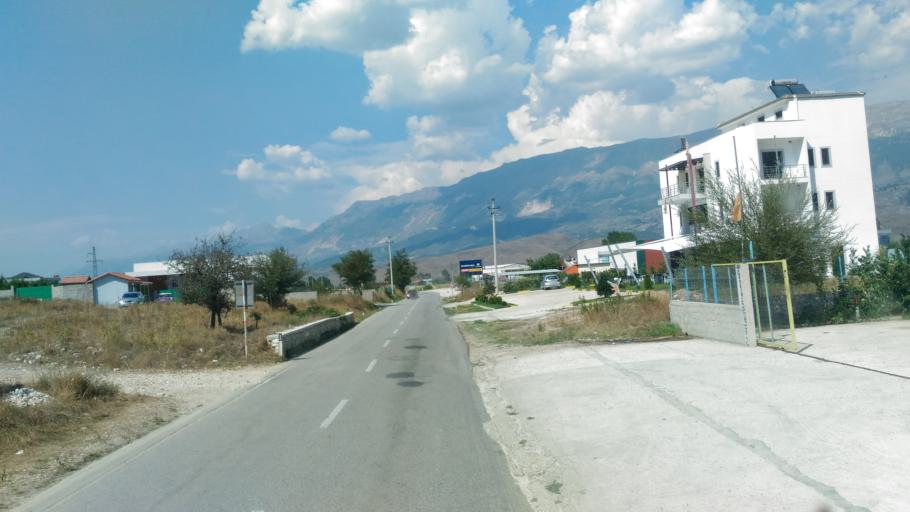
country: AL
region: Gjirokaster
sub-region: Rrethi i Gjirokastres
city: Dervician
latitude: 40.0496
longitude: 20.1771
